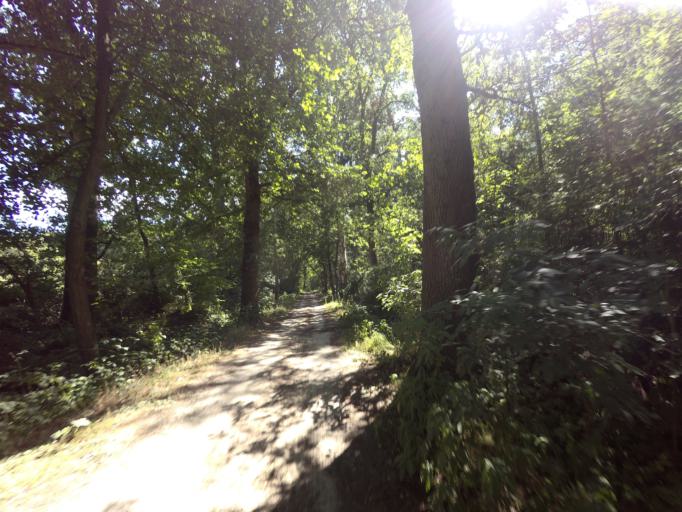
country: NL
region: Utrecht
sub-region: Gemeente De Bilt
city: De Bilt
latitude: 52.1427
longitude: 5.1902
